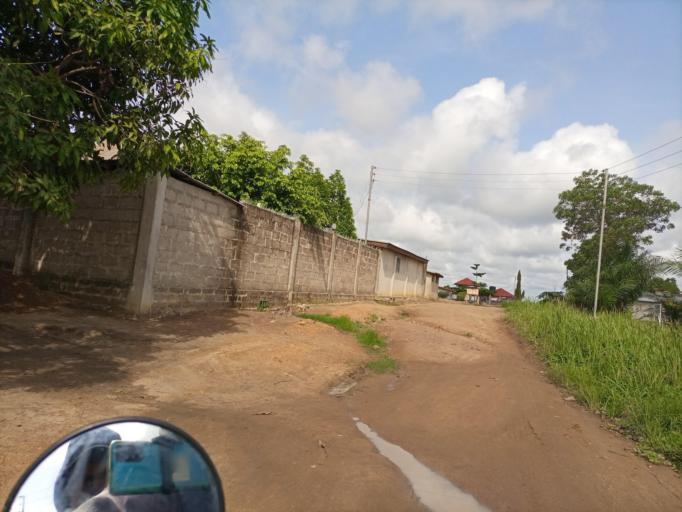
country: SL
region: Southern Province
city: Bo
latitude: 7.9669
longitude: -11.7673
